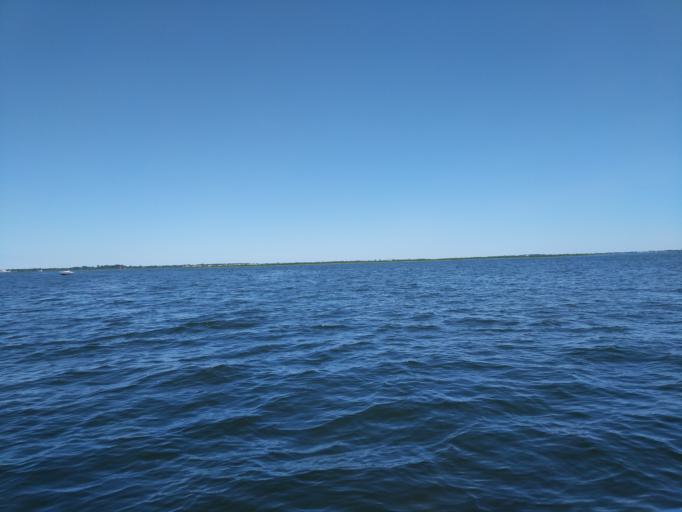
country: US
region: New York
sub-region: Nassau County
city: Barnum Island
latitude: 40.5984
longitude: -73.6383
